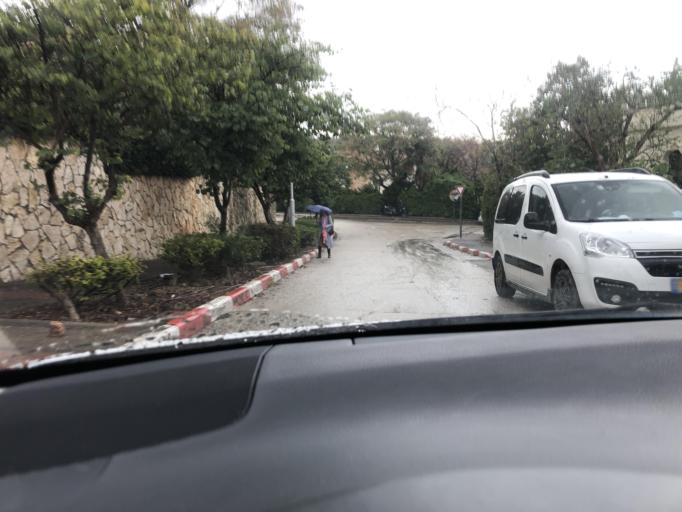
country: PS
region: West Bank
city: Azun Atme
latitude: 32.1103
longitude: 35.0317
